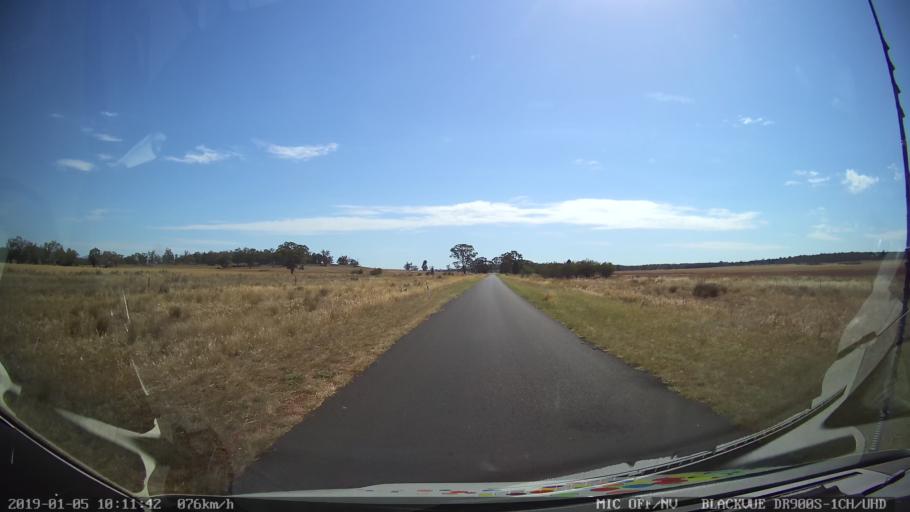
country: AU
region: New South Wales
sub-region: Gilgandra
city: Gilgandra
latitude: -31.6118
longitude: 148.9044
